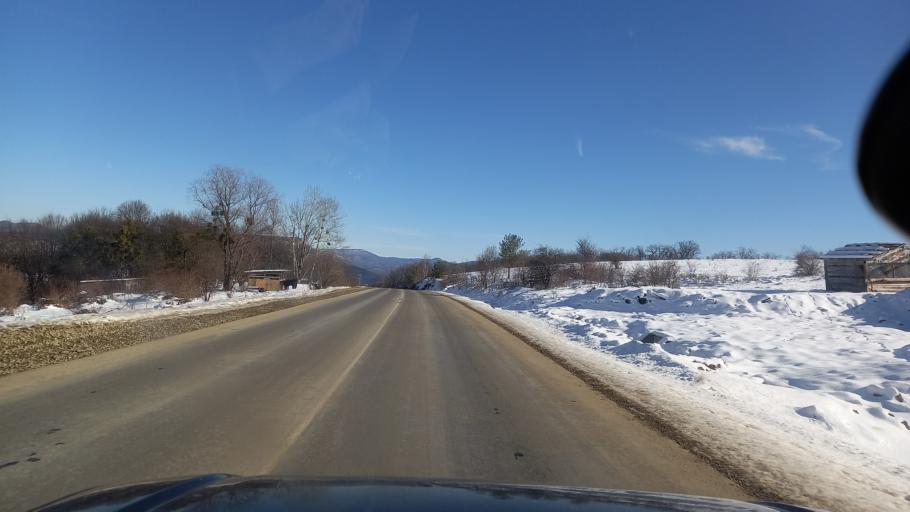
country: RU
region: Adygeya
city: Kamennomostskiy
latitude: 44.2311
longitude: 40.1300
